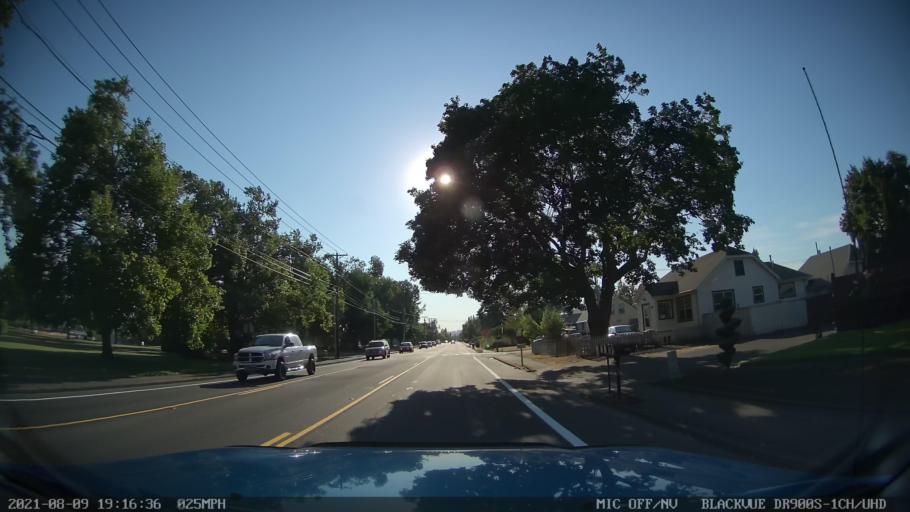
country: US
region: Oregon
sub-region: Marion County
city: Four Corners
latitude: 44.9399
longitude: -122.9958
